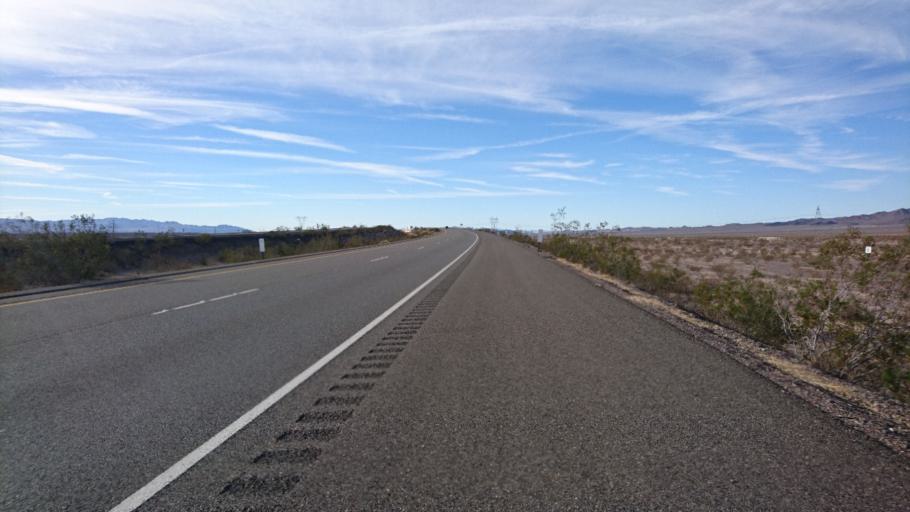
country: US
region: California
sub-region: San Bernardino County
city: Fort Irwin
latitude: 34.7707
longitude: -116.3629
